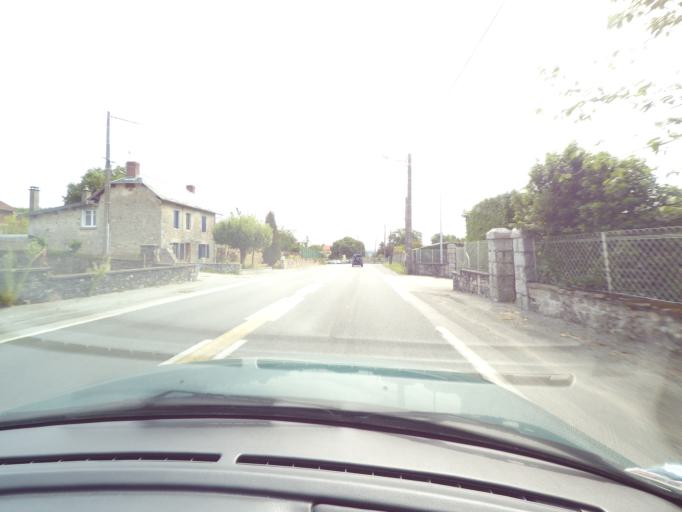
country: FR
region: Limousin
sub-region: Departement de la Haute-Vienne
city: Saint-Paul
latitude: 45.7965
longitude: 1.4239
